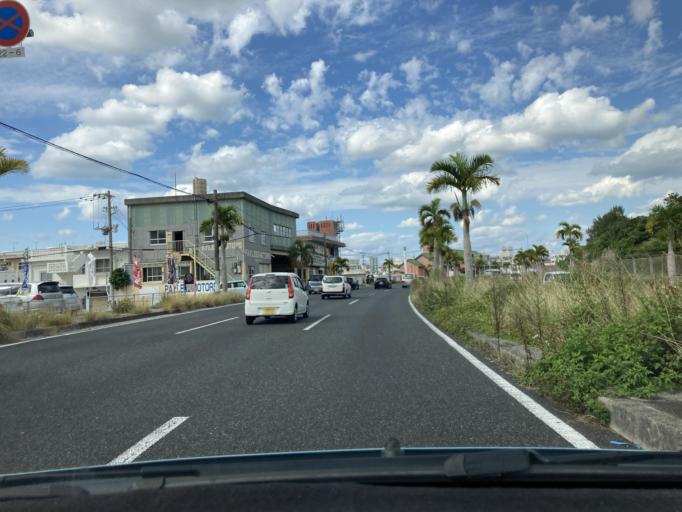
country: JP
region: Okinawa
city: Chatan
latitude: 26.3538
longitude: 127.7457
